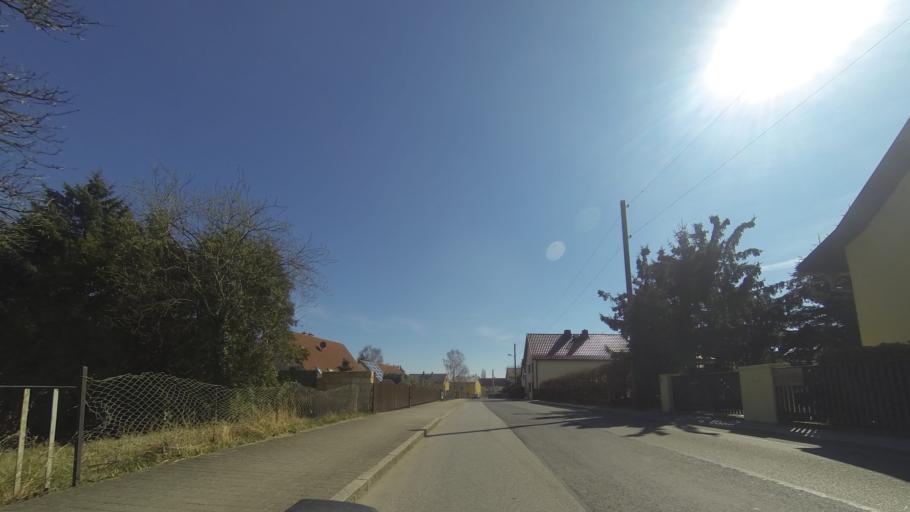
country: DE
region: Saxony
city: Ottendorf-Okrilla
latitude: 51.1511
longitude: 13.7952
